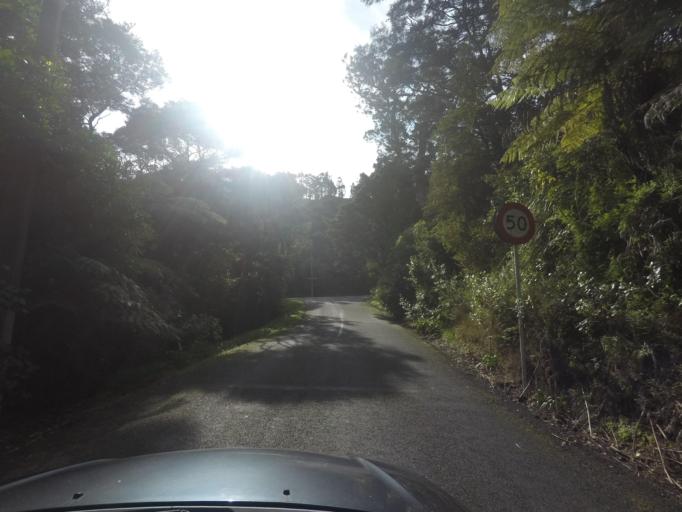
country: NZ
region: Auckland
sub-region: Auckland
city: Titirangi
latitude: -36.9383
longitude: 174.6418
